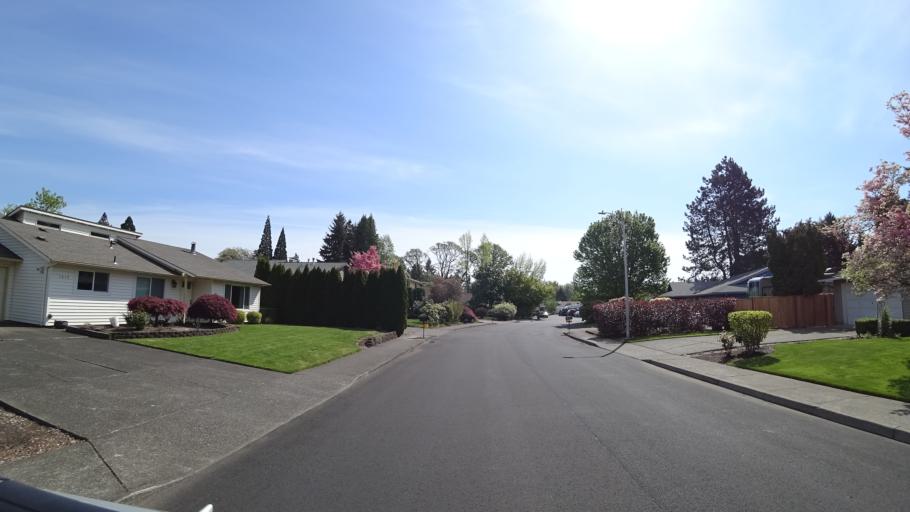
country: US
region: Oregon
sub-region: Washington County
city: Hillsboro
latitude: 45.5225
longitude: -122.9424
